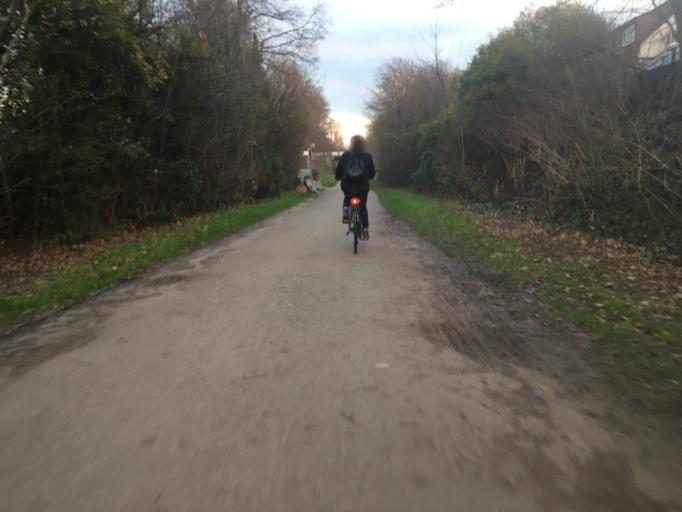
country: DE
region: North Rhine-Westphalia
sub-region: Regierungsbezirk Dusseldorf
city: Essen
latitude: 51.4611
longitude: 6.9614
